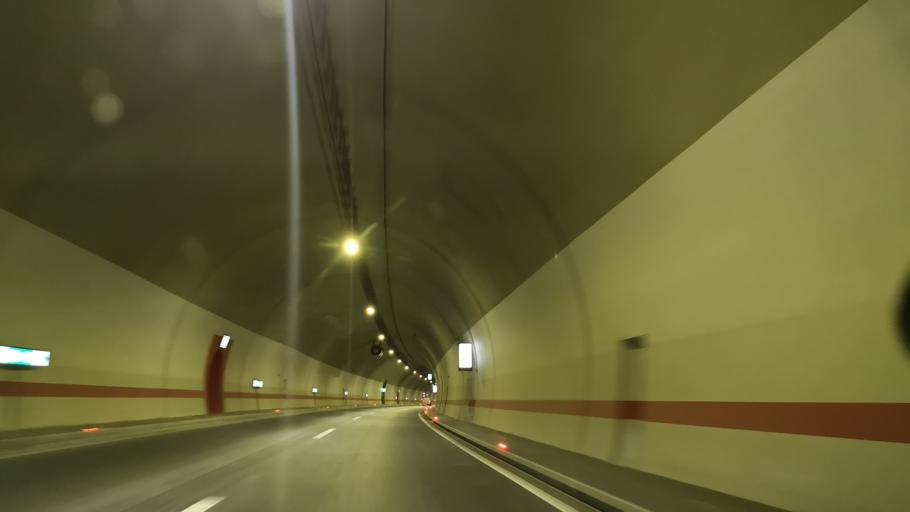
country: RS
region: Central Serbia
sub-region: Kolubarski Okrug
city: Ljig
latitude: 44.2057
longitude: 20.2645
